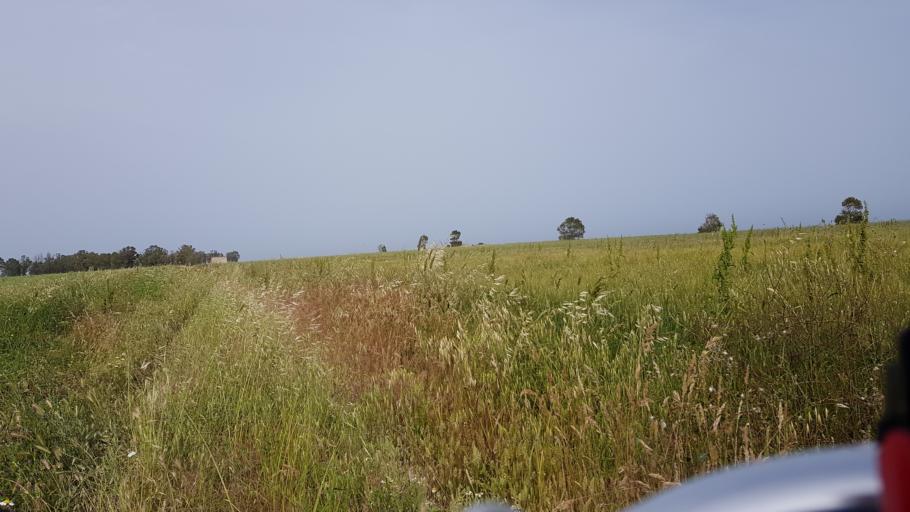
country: IT
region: Apulia
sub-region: Provincia di Brindisi
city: La Rosa
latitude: 40.5790
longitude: 18.0312
